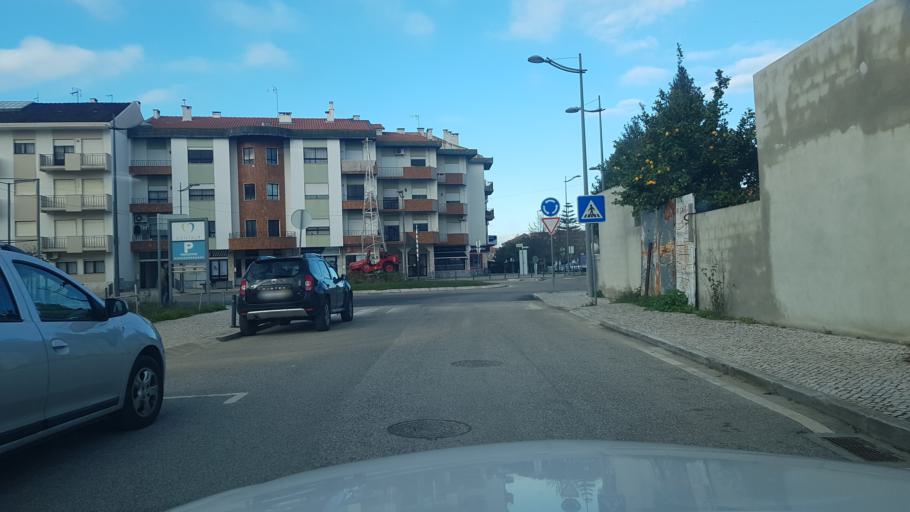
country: PT
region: Santarem
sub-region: Entroncamento
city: Entroncamento
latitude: 39.4649
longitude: -8.4733
